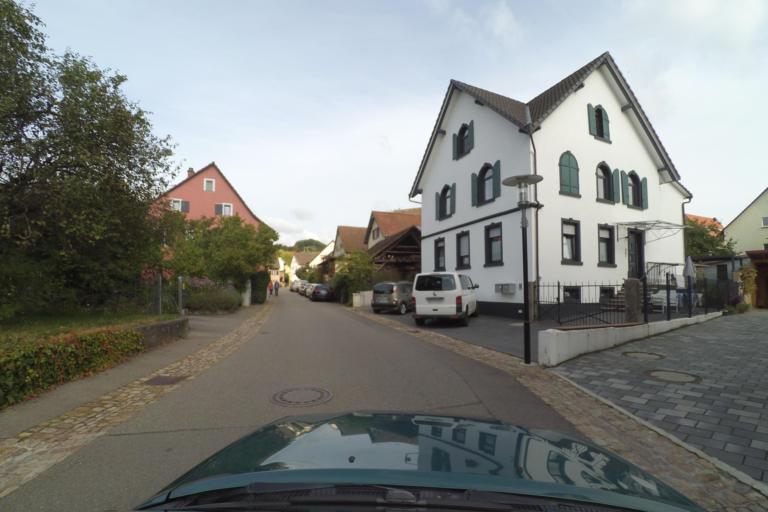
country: DE
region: Baden-Wuerttemberg
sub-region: Freiburg Region
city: Kandern
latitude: 47.7151
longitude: 7.6598
